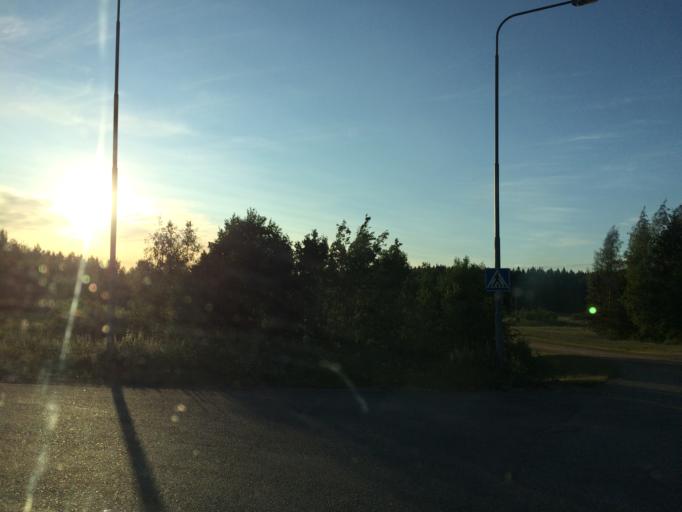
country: FI
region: Haeme
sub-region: Riihimaeki
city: Riihimaeki
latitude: 60.7528
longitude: 24.7377
